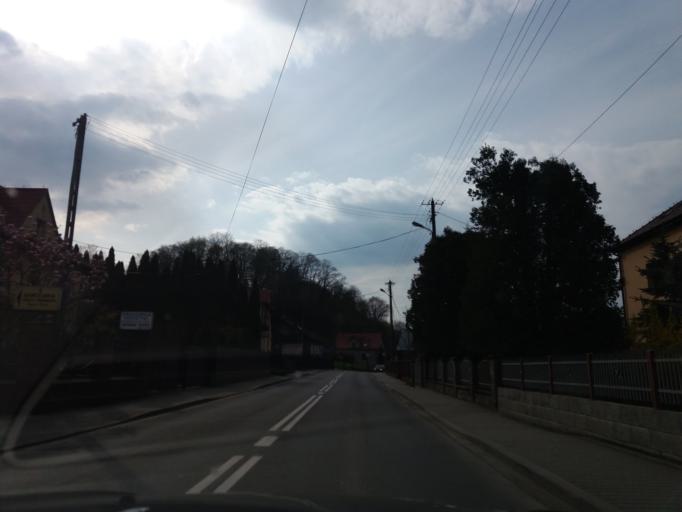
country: PL
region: Lesser Poland Voivodeship
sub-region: Powiat myslenicki
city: Dobczyce
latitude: 49.8780
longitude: 20.0962
